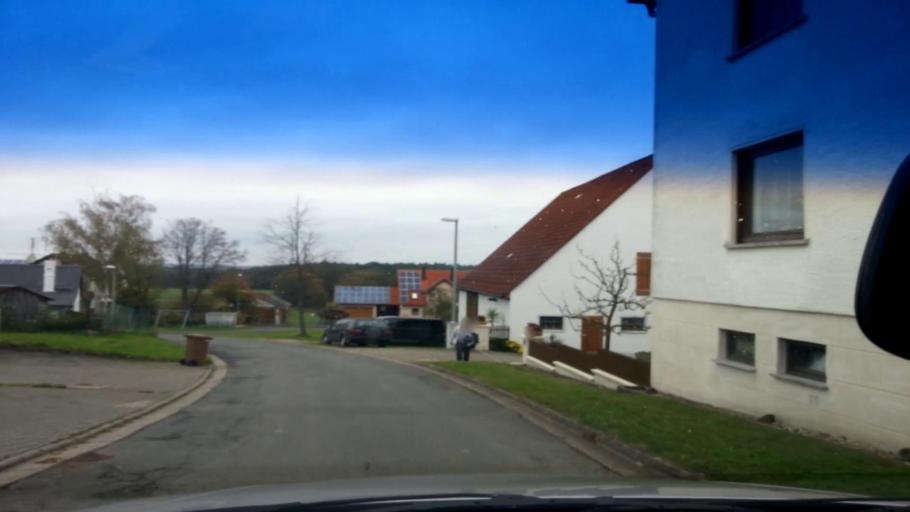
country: DE
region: Bavaria
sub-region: Upper Franconia
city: Burgebrach
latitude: 49.8056
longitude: 10.7785
